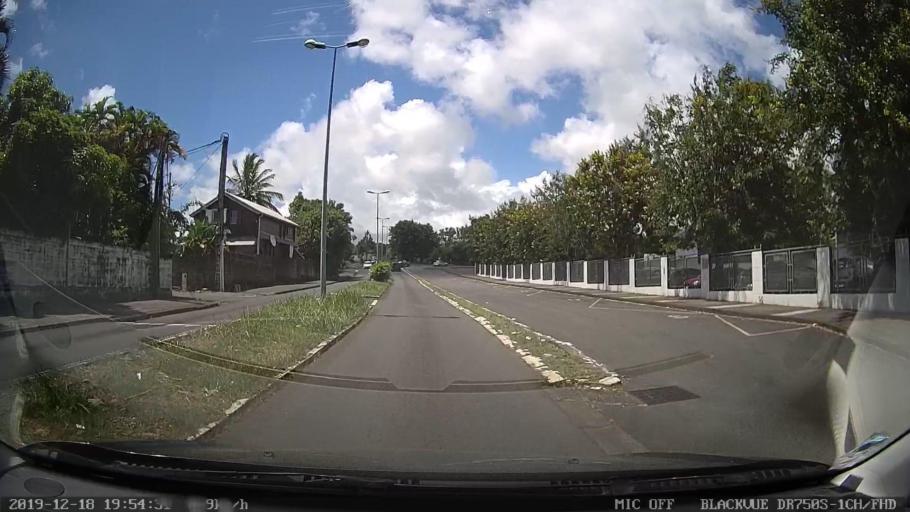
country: RE
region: Reunion
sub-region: Reunion
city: Saint-Andre
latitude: -20.9336
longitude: 55.6380
